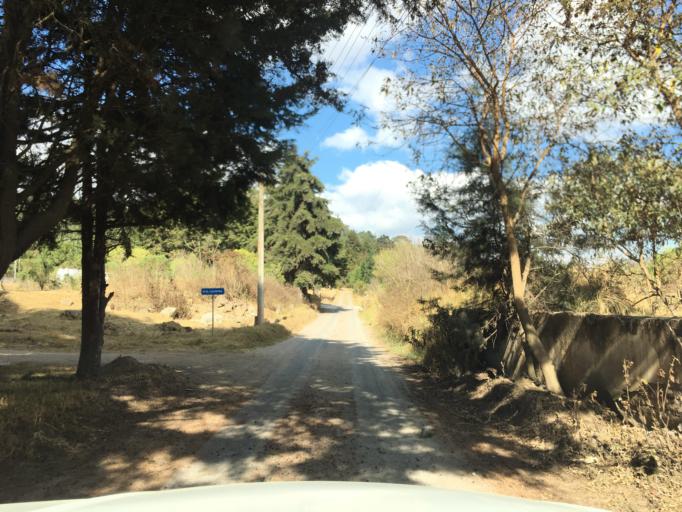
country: GT
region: Quetzaltenango
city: Quetzaltenango
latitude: 14.8436
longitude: -91.4951
